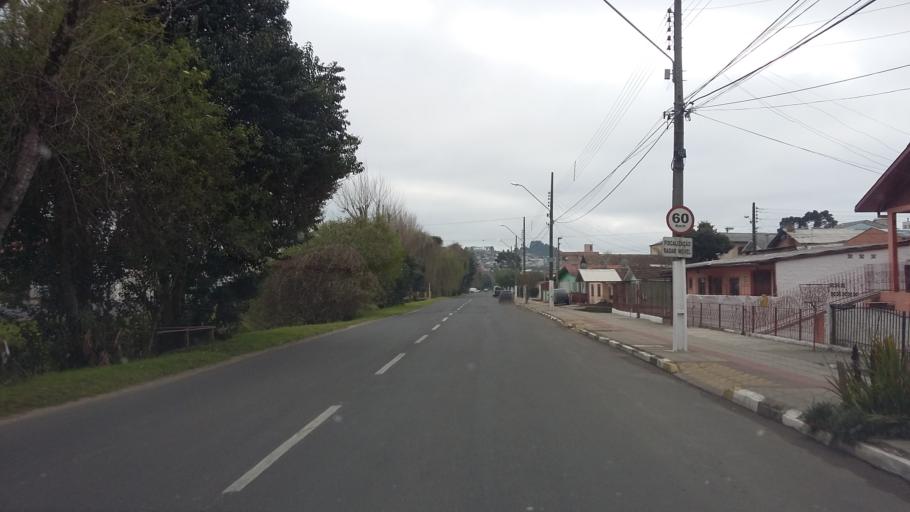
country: BR
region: Santa Catarina
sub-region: Lages
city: Lages
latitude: -27.8222
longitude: -50.3389
